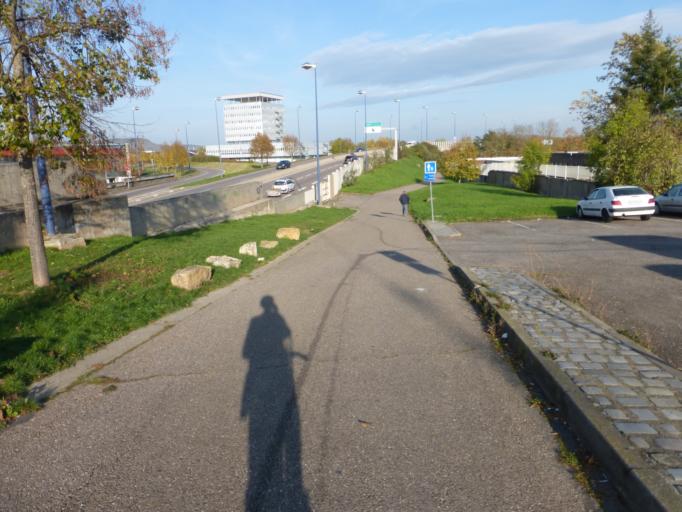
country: FR
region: Lorraine
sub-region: Departement de Meurthe-et-Moselle
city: Jarville-la-Malgrange
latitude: 48.6759
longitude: 6.2002
